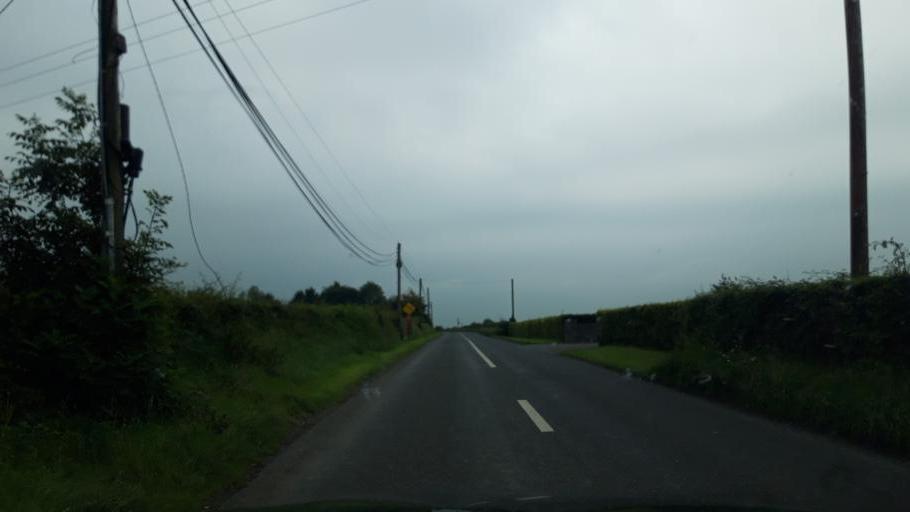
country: IE
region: Munster
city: Fethard
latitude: 52.4867
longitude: -7.6927
